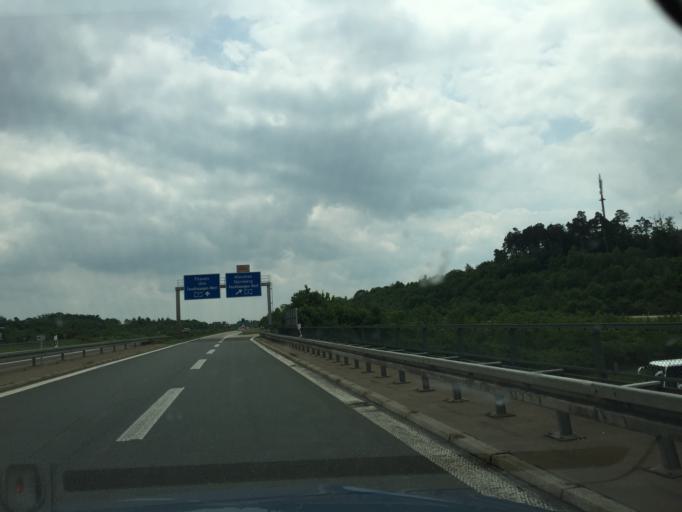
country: DE
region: Bavaria
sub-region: Regierungsbezirk Mittelfranken
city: Schnelldorf
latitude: 49.2032
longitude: 10.2334
